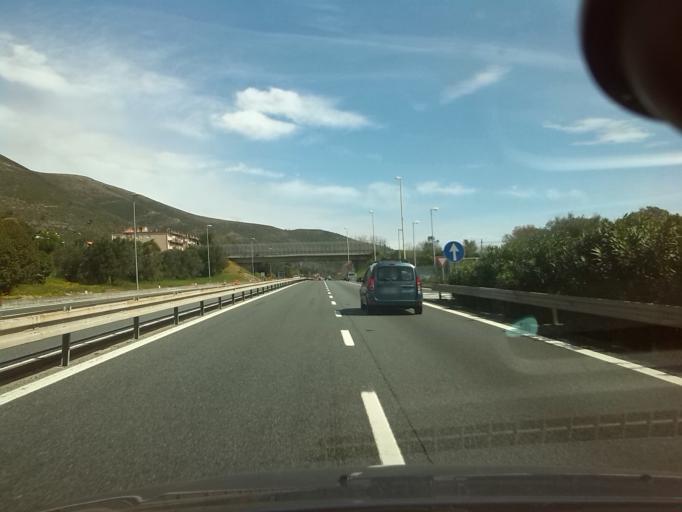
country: IT
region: Liguria
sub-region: Provincia di Savona
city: Campochiesa
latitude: 44.0890
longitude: 8.2074
